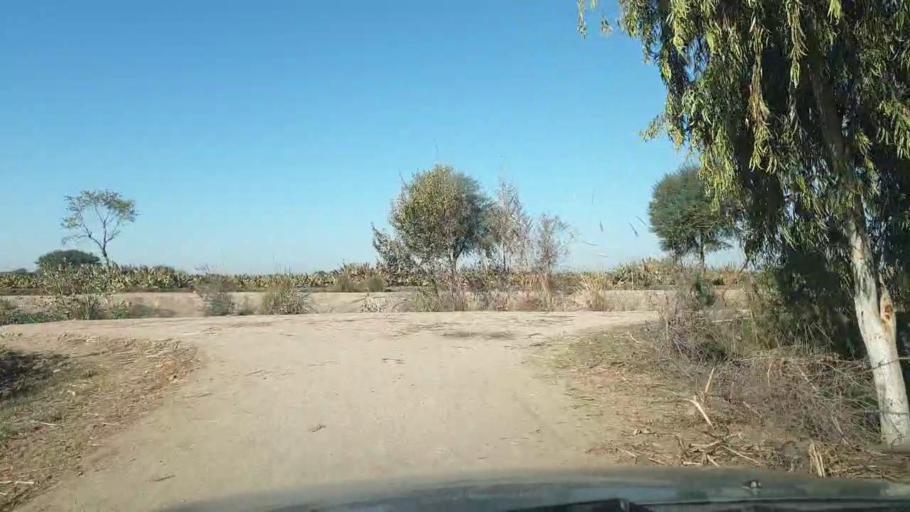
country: PK
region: Sindh
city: Ghotki
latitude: 28.0174
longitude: 69.2692
